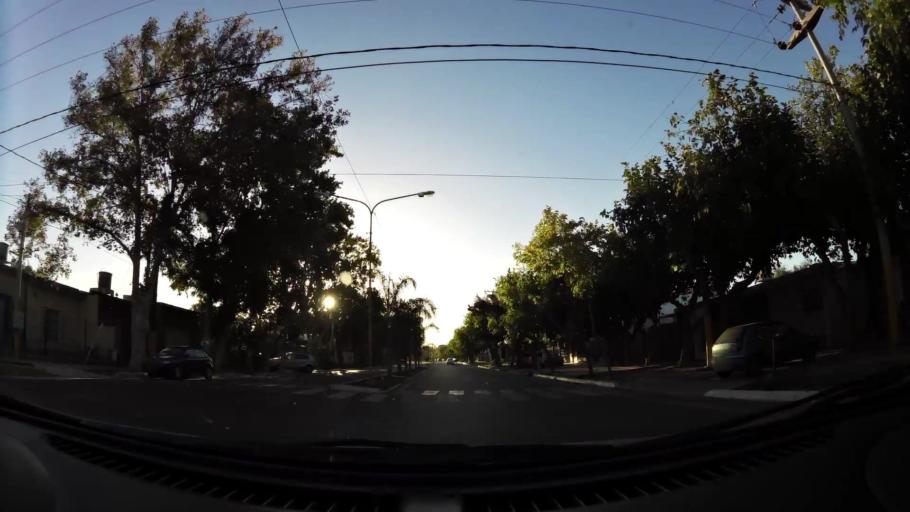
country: AR
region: San Juan
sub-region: Departamento de Santa Lucia
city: Santa Lucia
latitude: -31.5423
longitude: -68.4913
